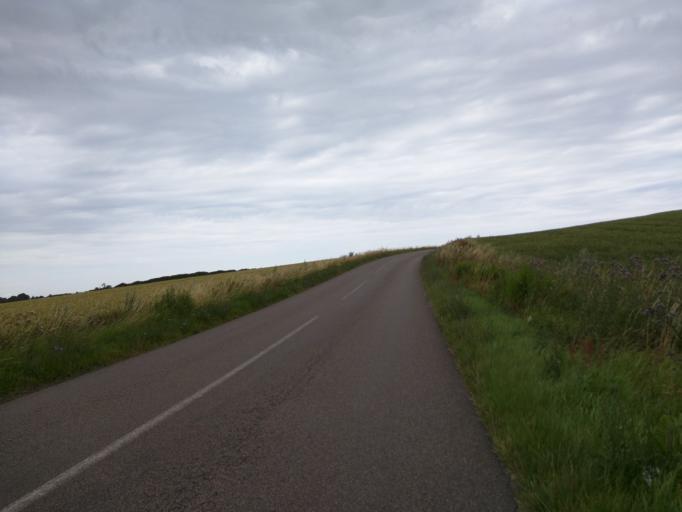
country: DK
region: Zealand
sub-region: Kalundborg Kommune
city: Svebolle
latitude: 55.7064
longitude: 11.3036
